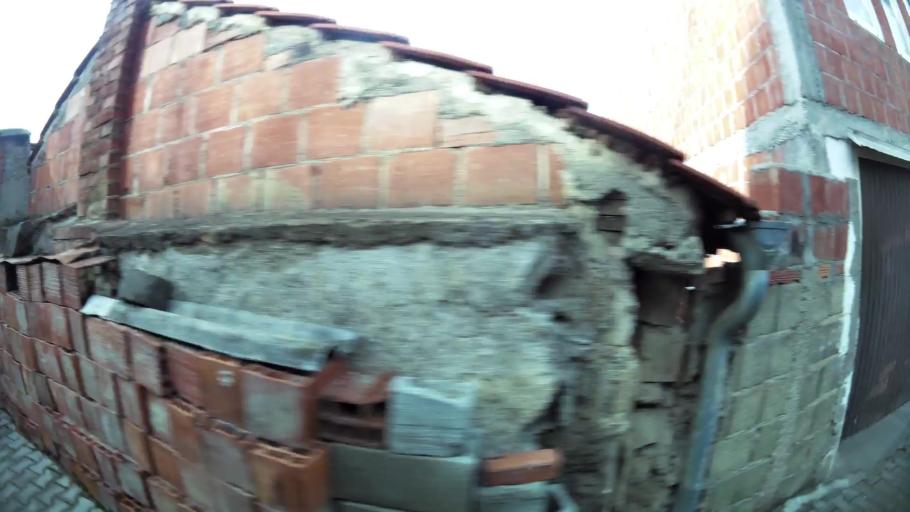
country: XK
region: Pristina
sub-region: Komuna e Prishtines
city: Pristina
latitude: 42.6764
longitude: 21.1761
